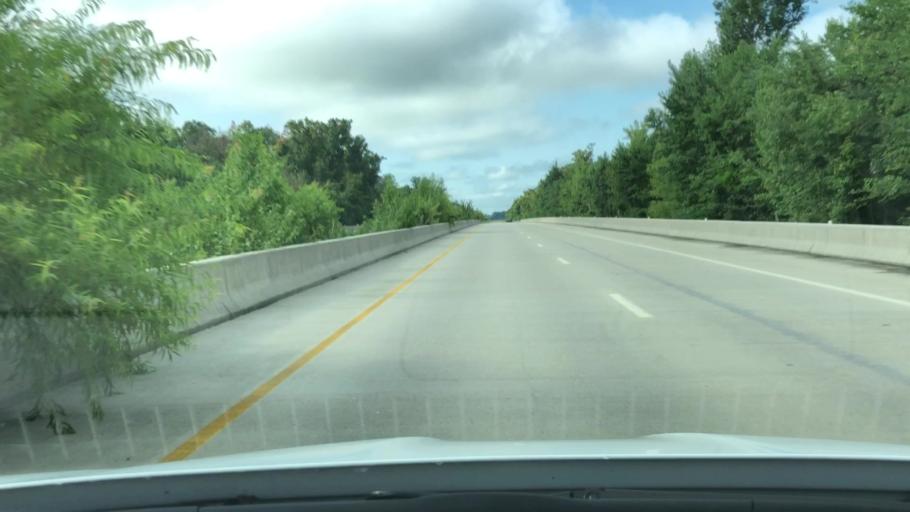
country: US
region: Virginia
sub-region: City of Portsmouth
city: Portsmouth Heights
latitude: 36.6336
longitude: -76.3635
